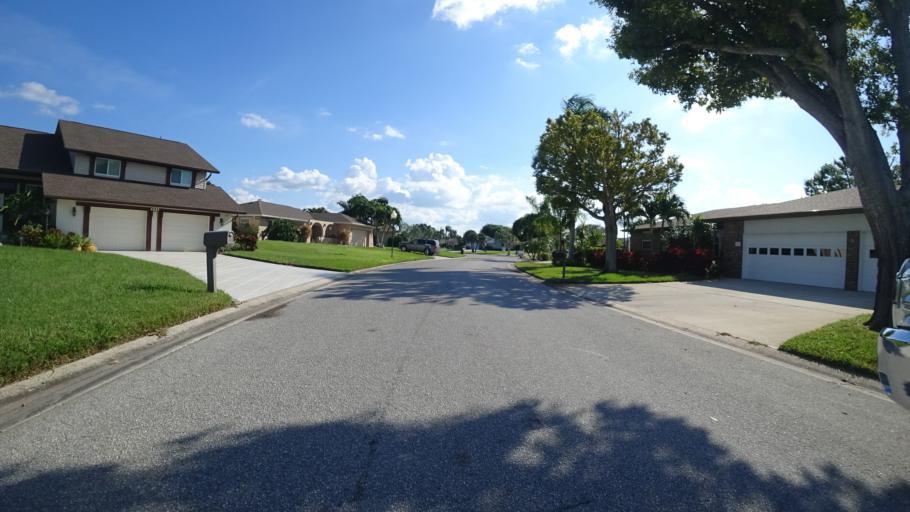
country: US
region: Florida
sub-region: Manatee County
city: Cortez
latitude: 27.4580
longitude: -82.6516
